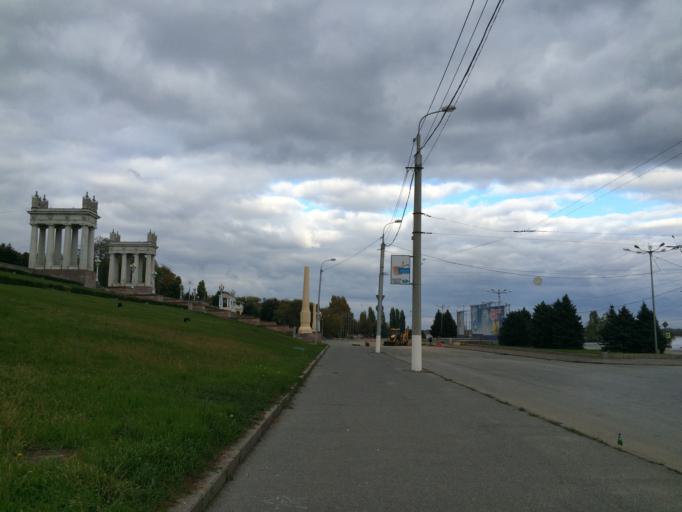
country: RU
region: Volgograd
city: Volgograd
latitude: 48.7029
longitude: 44.5203
